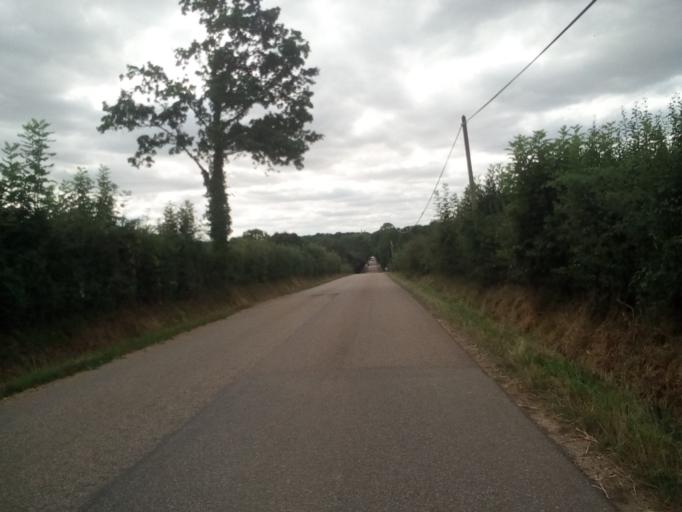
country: FR
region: Lower Normandy
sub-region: Departement du Calvados
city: Troarn
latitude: 49.1662
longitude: -0.1449
